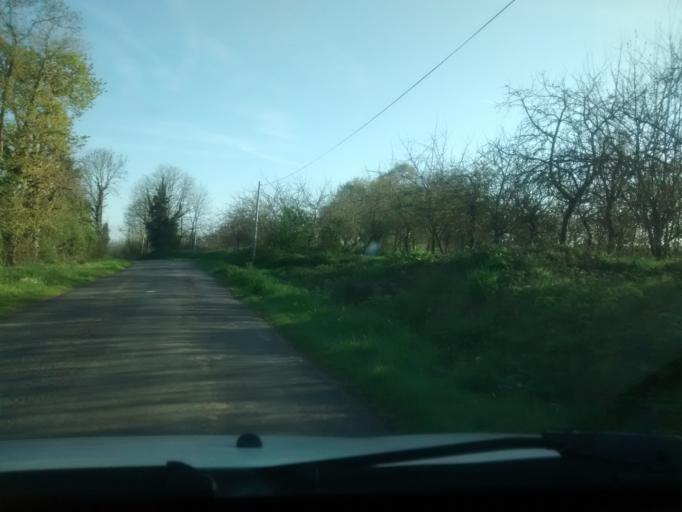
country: FR
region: Brittany
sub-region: Departement d'Ille-et-Vilaine
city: Saint-Broladre
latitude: 48.5750
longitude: -1.6438
